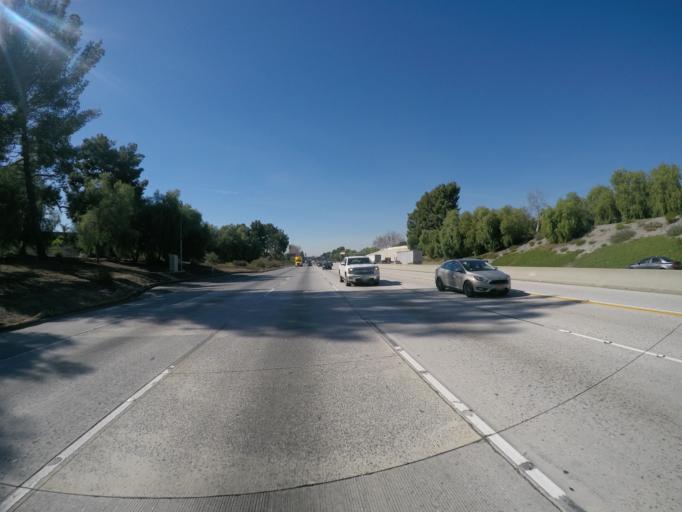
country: US
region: California
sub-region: Los Angeles County
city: Citrus
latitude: 34.1208
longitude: -117.8920
